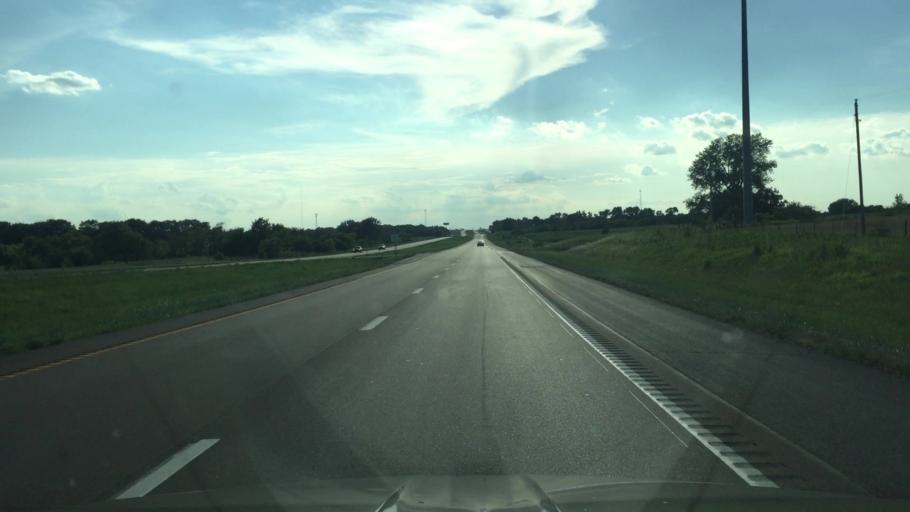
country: US
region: Missouri
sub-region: Pettis County
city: La Monte
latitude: 38.7624
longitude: -93.3981
